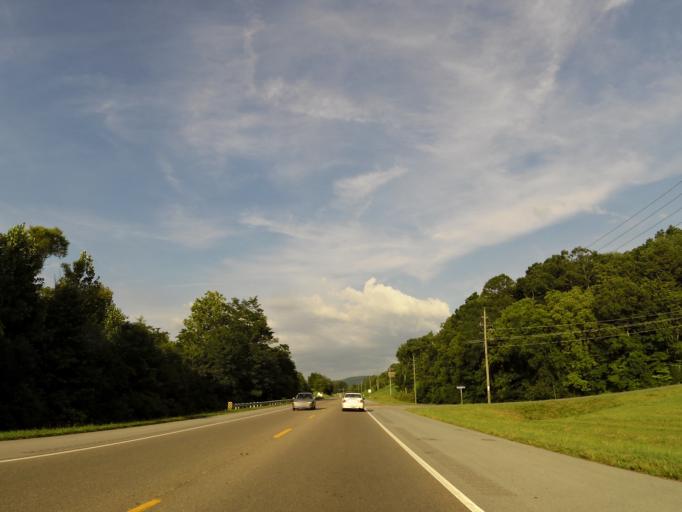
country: US
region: Tennessee
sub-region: Sevier County
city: Sevierville
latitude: 35.8825
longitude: -83.4672
